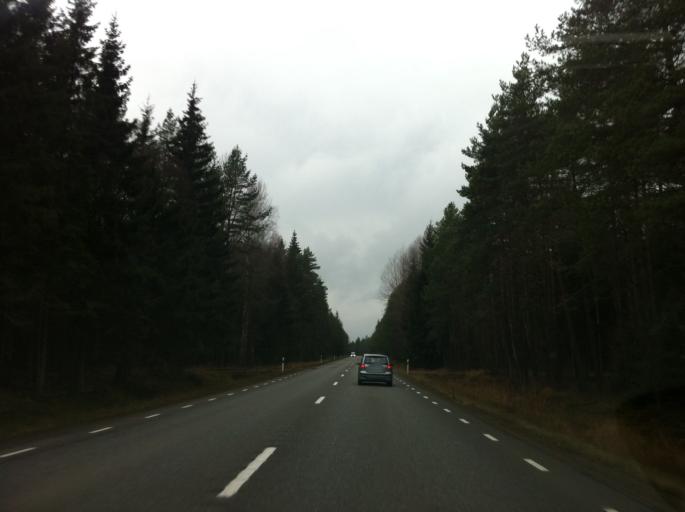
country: SE
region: Joenkoeping
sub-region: Vetlanda Kommun
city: Landsbro
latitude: 57.4082
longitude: 14.9793
